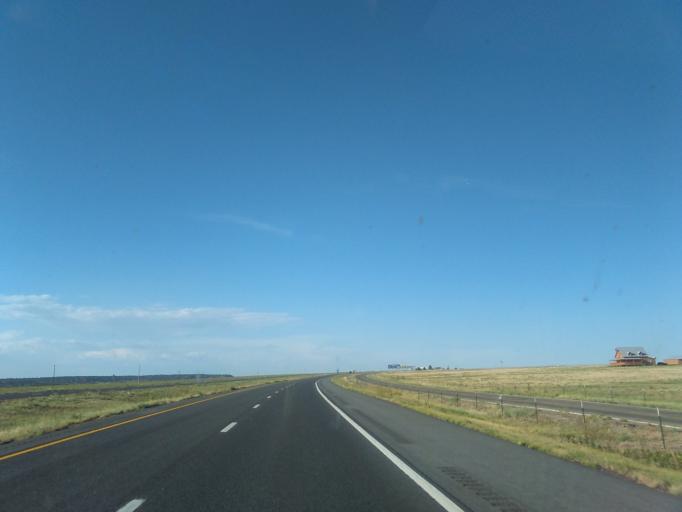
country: US
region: New Mexico
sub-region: San Miguel County
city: Las Vegas
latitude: 35.6637
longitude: -105.1856
